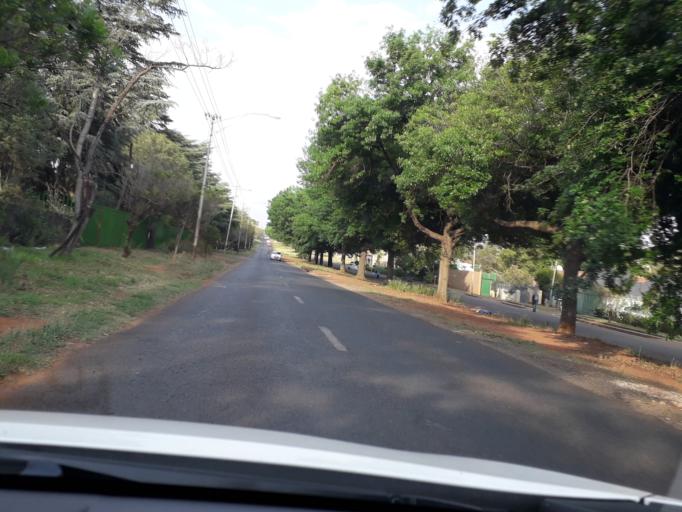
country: ZA
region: Gauteng
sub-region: City of Johannesburg Metropolitan Municipality
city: Johannesburg
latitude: -26.1603
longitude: 27.9902
